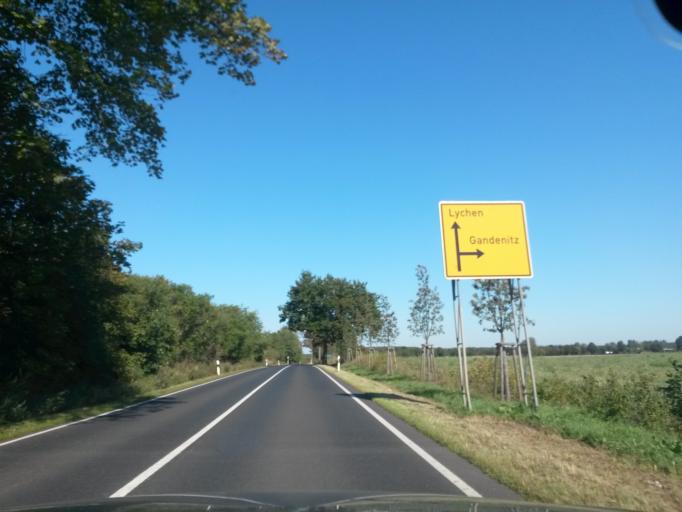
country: DE
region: Brandenburg
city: Templin
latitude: 53.1369
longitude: 13.4801
